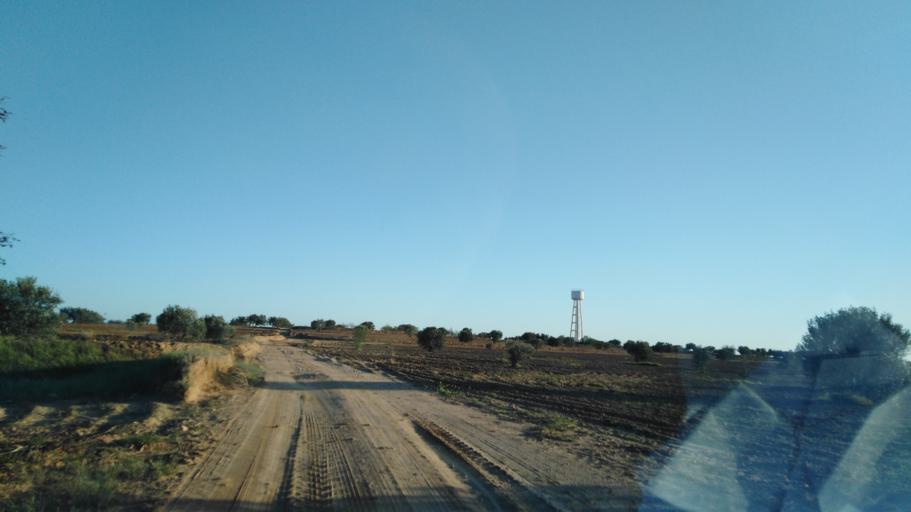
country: TN
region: Safaqis
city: Bi'r `Ali Bin Khalifah
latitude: 34.6730
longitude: 10.3834
